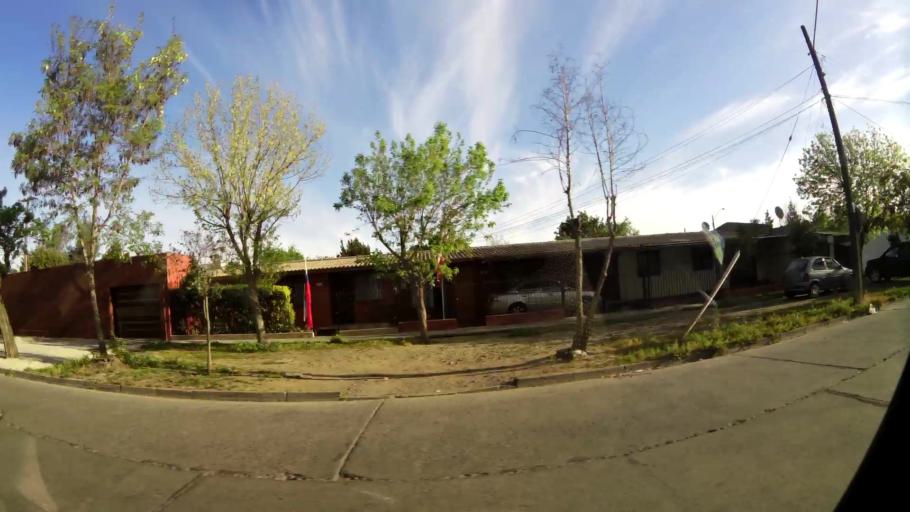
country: CL
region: Santiago Metropolitan
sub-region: Provincia de Santiago
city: Lo Prado
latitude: -33.4372
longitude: -70.7175
